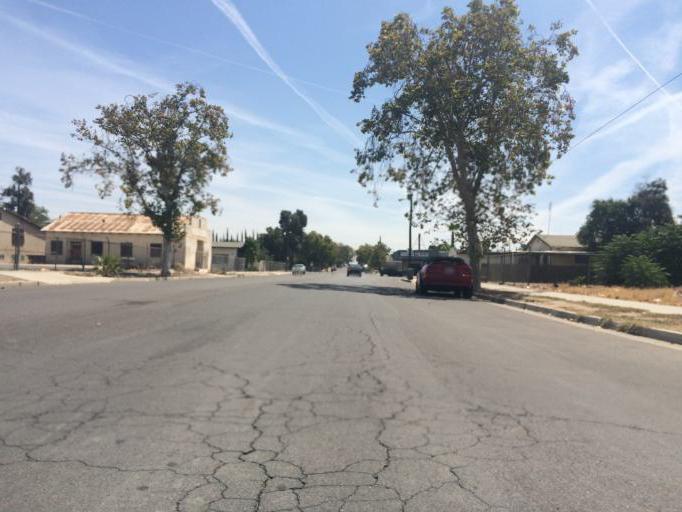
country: US
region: California
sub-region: Fresno County
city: Fresno
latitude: 36.7285
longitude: -119.8001
